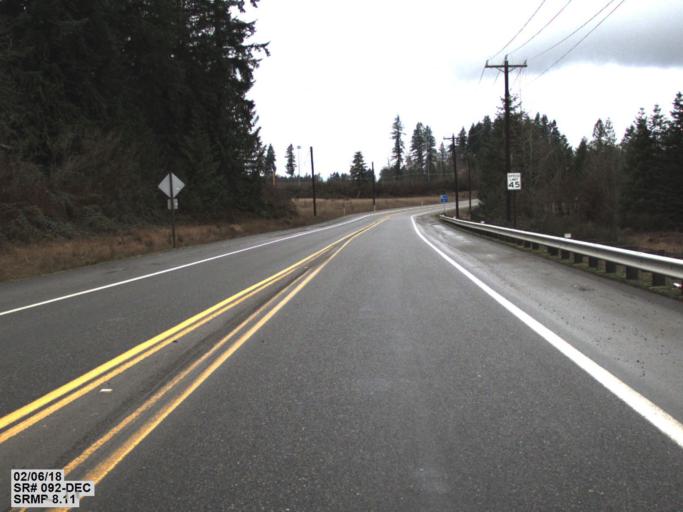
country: US
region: Washington
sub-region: Snohomish County
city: Granite Falls
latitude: 48.0911
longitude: -121.9820
